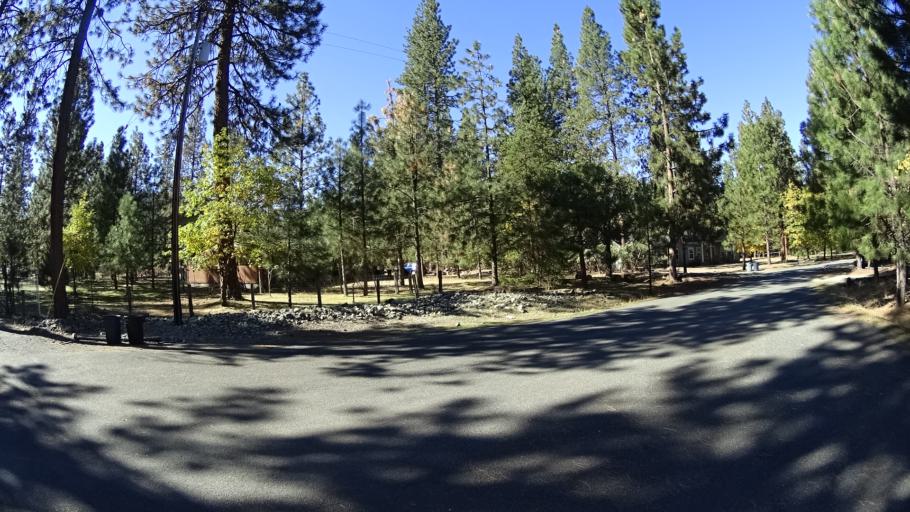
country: US
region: California
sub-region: Siskiyou County
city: Yreka
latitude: 41.5202
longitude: -122.9188
